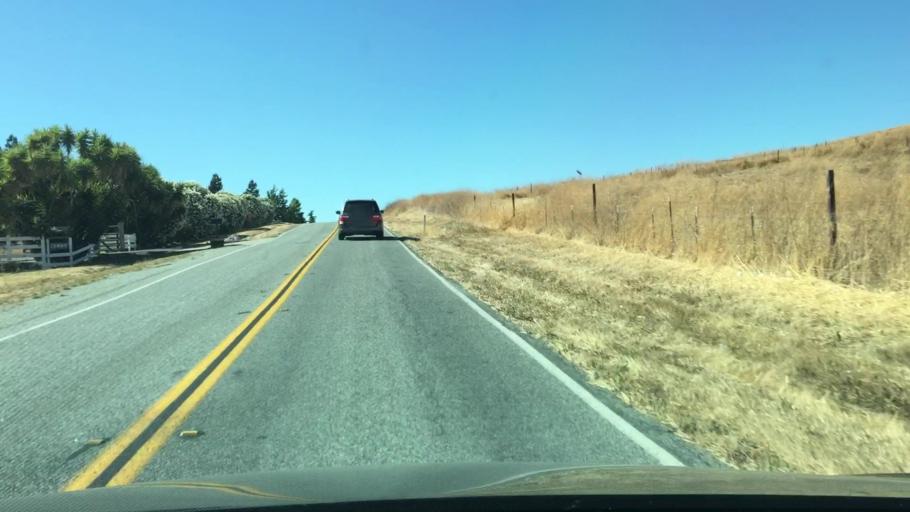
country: US
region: California
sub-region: Santa Clara County
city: San Martin
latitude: 37.0912
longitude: -121.5691
